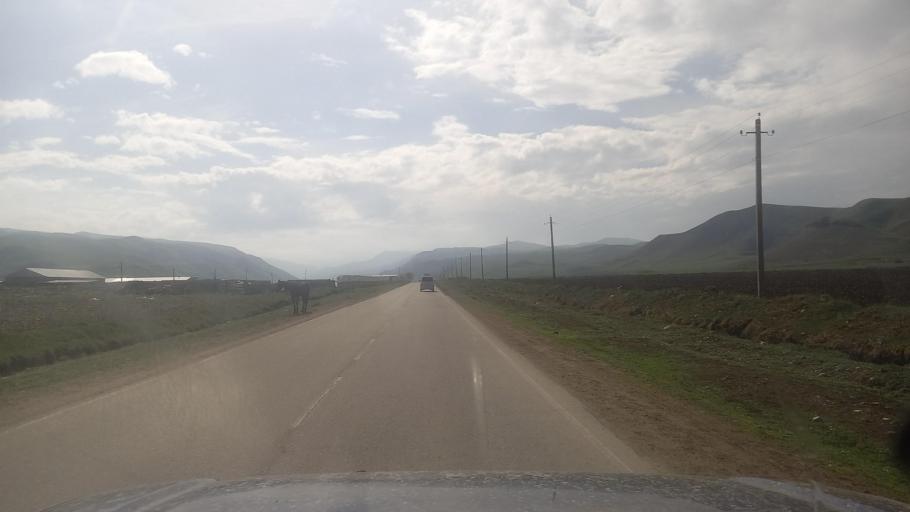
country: RU
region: Kabardino-Balkariya
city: Kamennomostskoye
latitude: 43.7359
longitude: 43.0138
